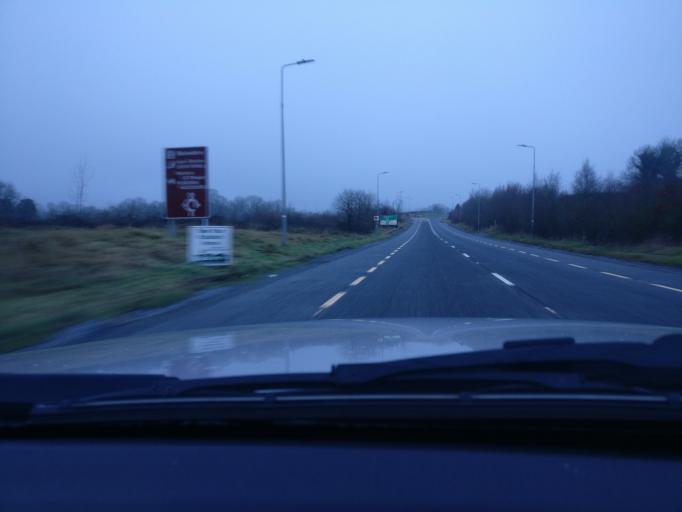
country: IE
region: Leinster
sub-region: An Iarmhi
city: Rochfortbridge
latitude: 53.3906
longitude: -7.3661
